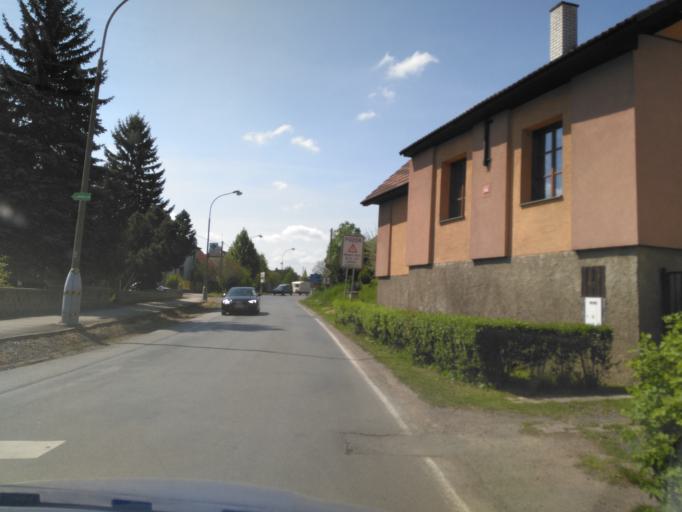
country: CZ
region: Central Bohemia
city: Lochovice
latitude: 49.8498
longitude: 13.9764
